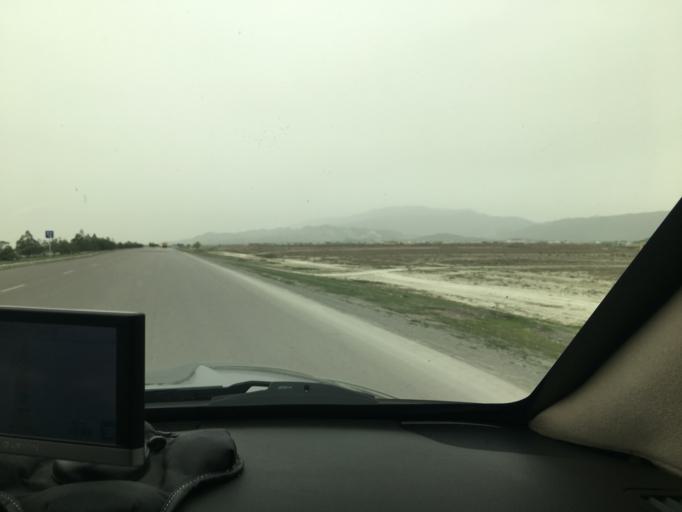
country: TM
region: Ahal
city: Baharly
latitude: 38.3114
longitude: 57.6121
